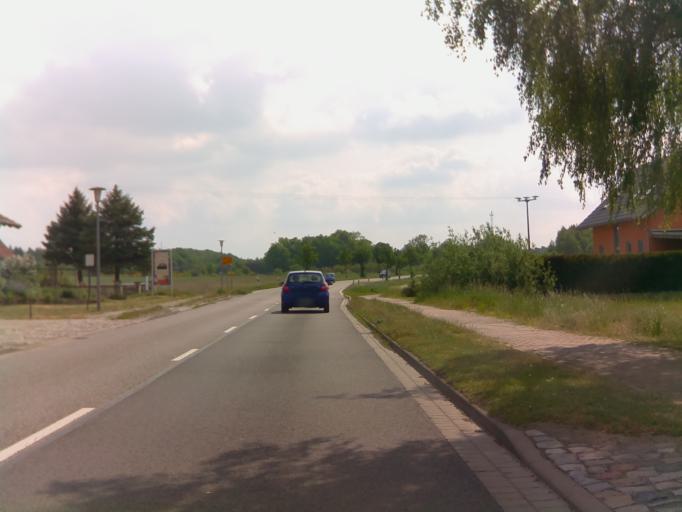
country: DE
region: Saxony-Anhalt
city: Javenitz
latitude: 52.5252
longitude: 11.4686
